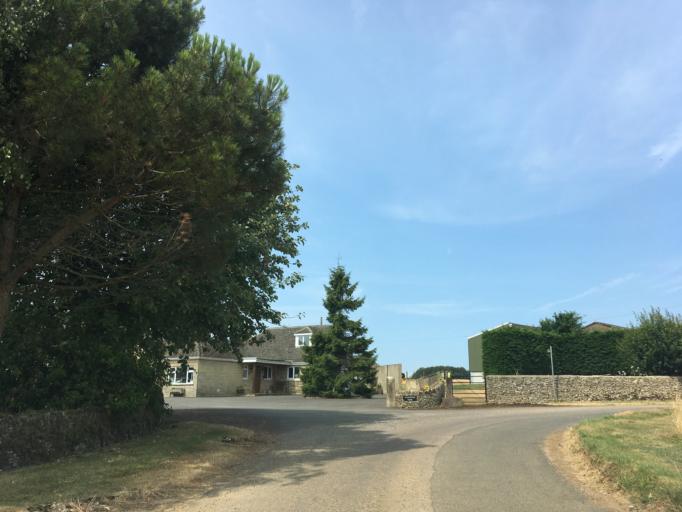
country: GB
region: England
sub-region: Gloucestershire
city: Nailsworth
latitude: 51.6610
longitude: -2.2424
